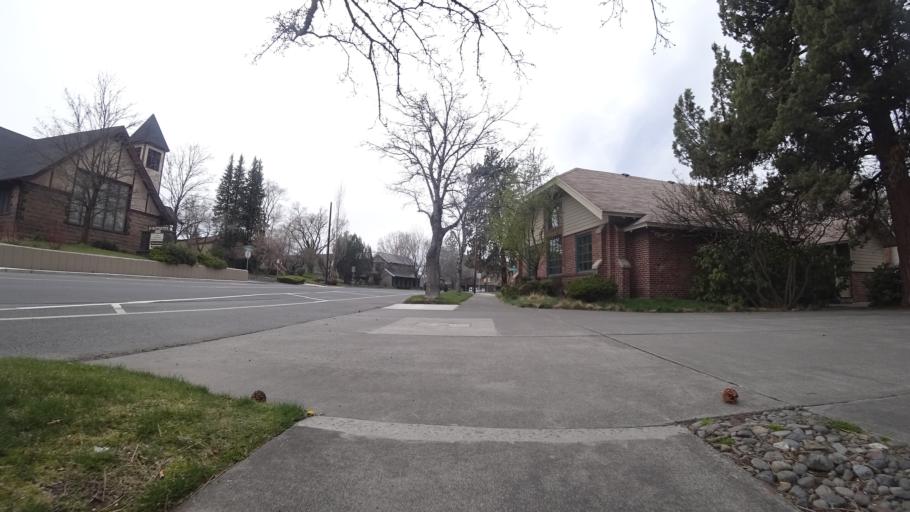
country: US
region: Oregon
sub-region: Deschutes County
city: Bend
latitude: 44.0560
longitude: -121.3093
